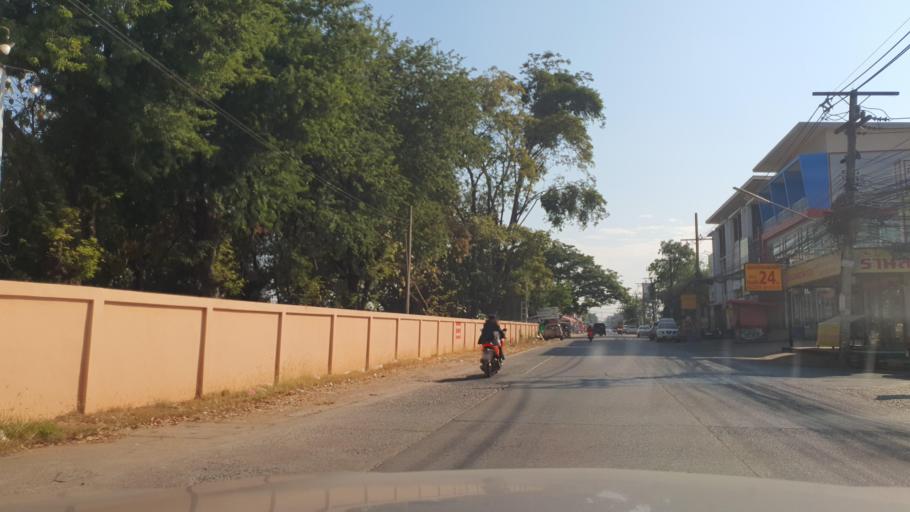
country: TH
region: Khon Kaen
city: Khon Kaen
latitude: 16.4213
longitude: 102.8081
